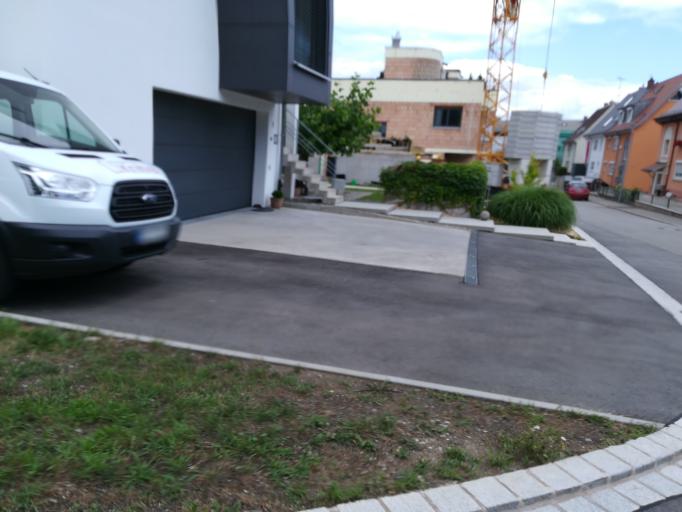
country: DE
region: Baden-Wuerttemberg
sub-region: Freiburg Region
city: Singen
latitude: 47.7564
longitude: 8.8320
